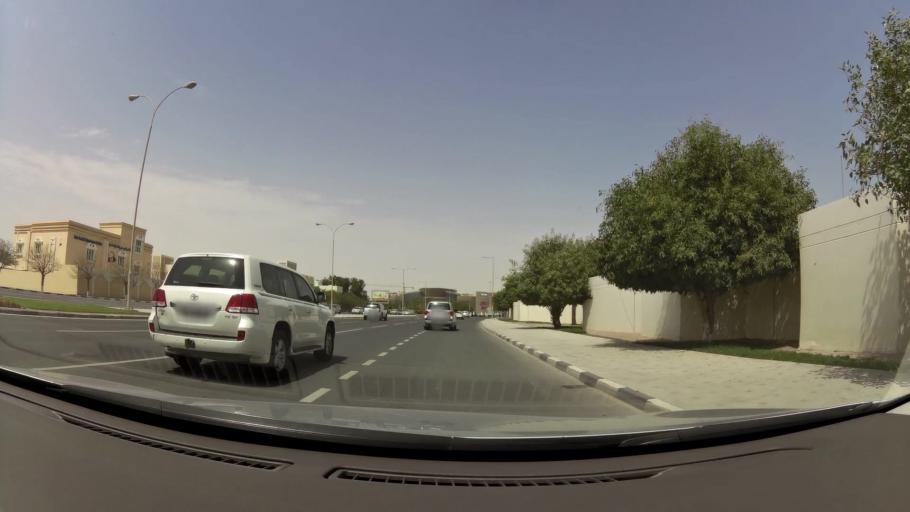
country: QA
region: Baladiyat ad Dawhah
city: Doha
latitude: 25.3315
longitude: 51.4827
